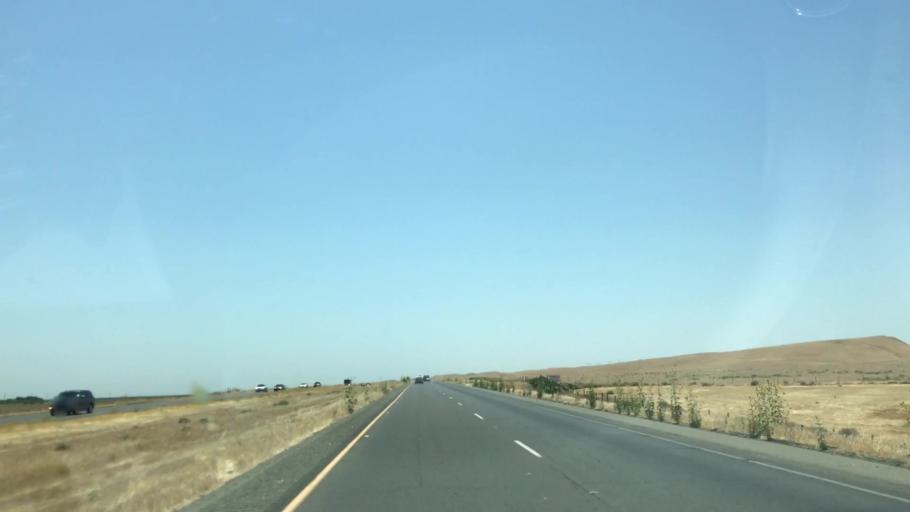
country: US
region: California
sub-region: Fresno County
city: Coalinga
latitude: 36.3492
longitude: -120.3171
